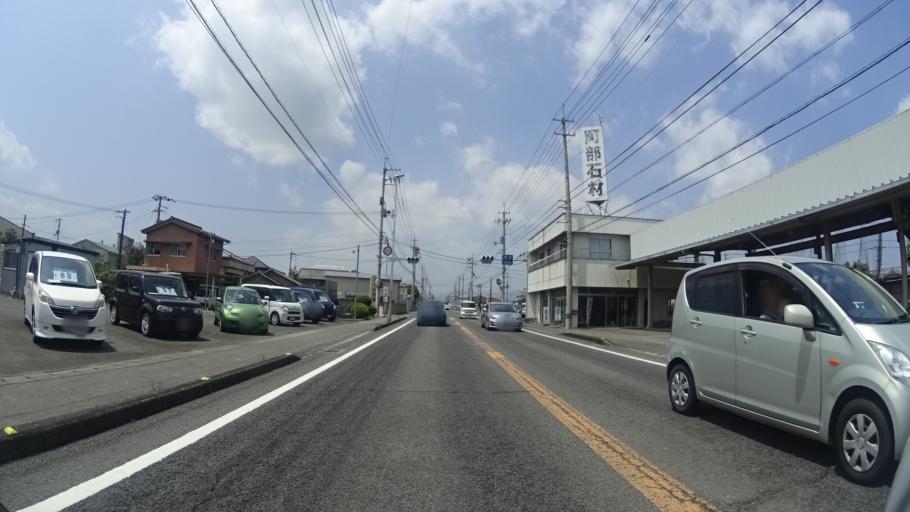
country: JP
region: Tokushima
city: Ishii
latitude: 34.0719
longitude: 134.3984
